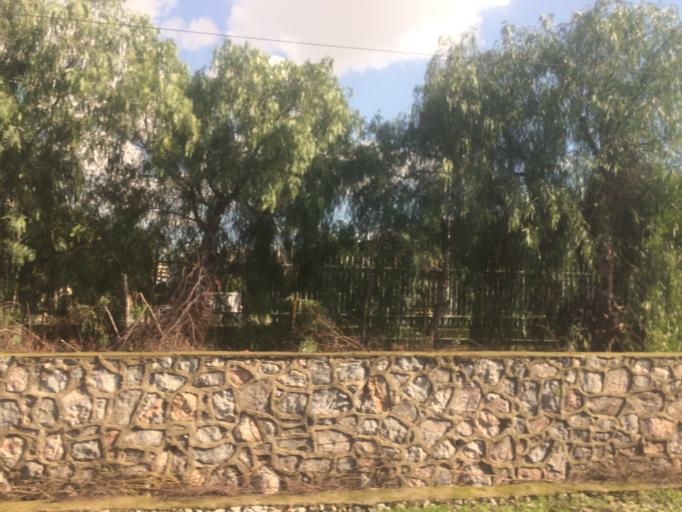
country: TR
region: Izmir
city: Buca
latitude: 38.4457
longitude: 27.1734
